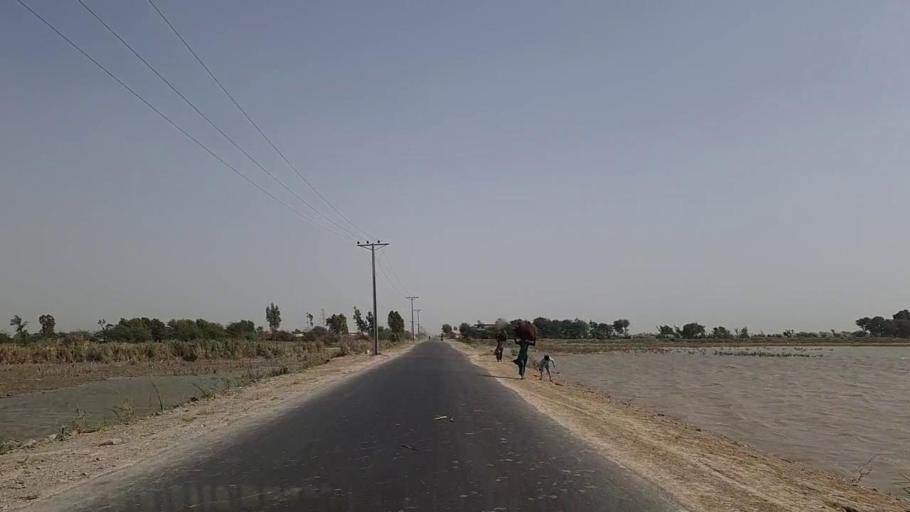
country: PK
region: Sindh
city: Tando Bago
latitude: 24.8052
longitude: 68.9357
